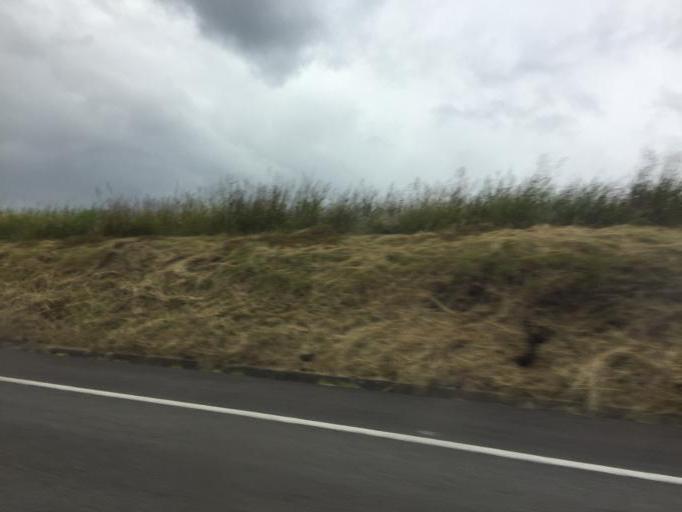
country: MX
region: Jalisco
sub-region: Zapotlan del Rey
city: Zapotlan del Rey
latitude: 20.4858
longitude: -102.9408
